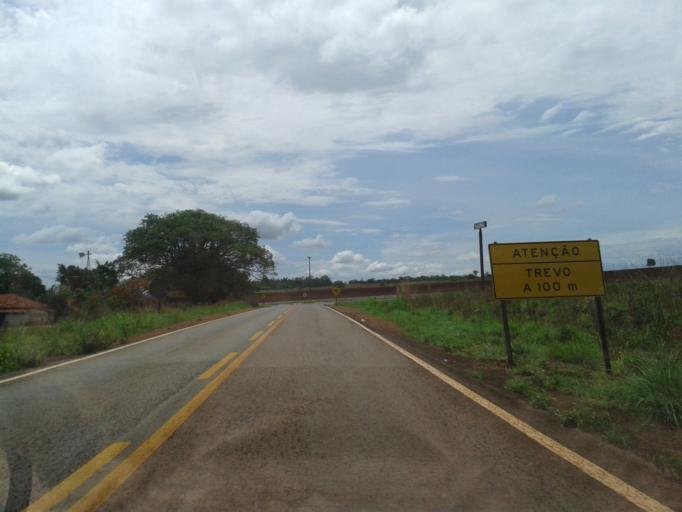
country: BR
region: Goias
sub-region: Goiatuba
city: Goiatuba
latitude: -18.1093
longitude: -49.2752
